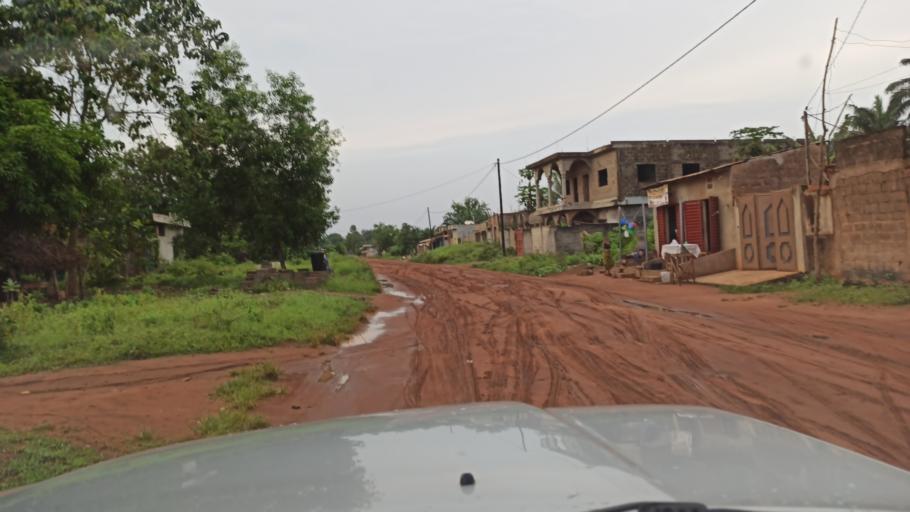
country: BJ
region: Queme
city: Porto-Novo
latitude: 6.4826
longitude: 2.6718
